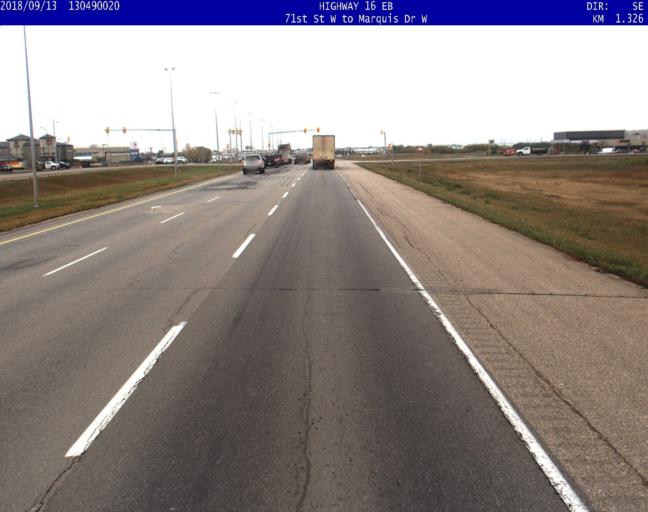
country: CA
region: Saskatchewan
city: Martensville
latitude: 52.1936
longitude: -106.6914
